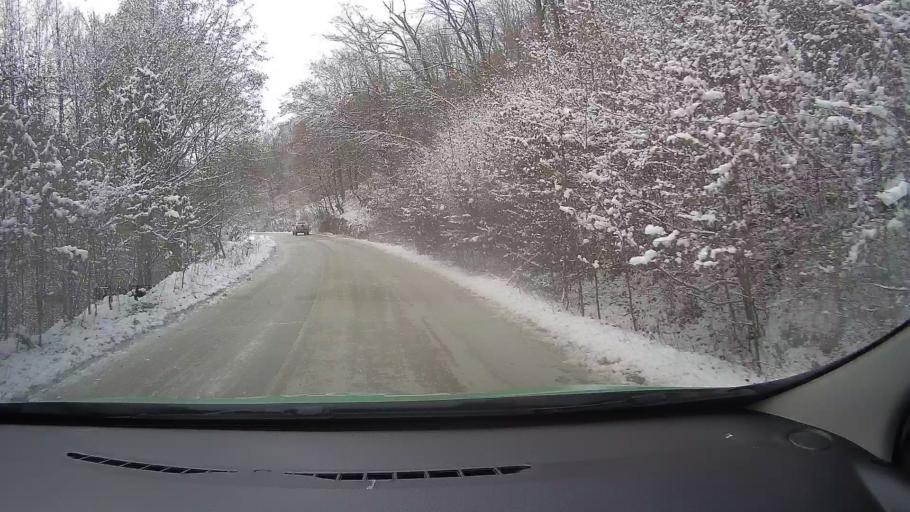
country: RO
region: Alba
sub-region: Oras Zlatna
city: Zlatna
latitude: 46.0981
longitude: 23.1842
